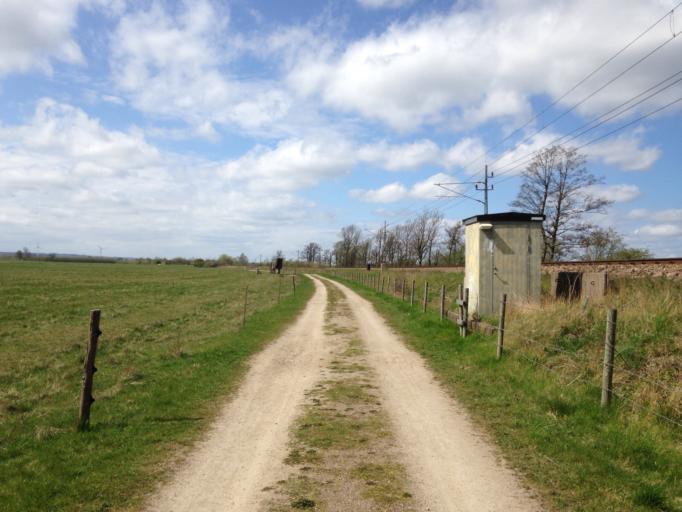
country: SE
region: Skane
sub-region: Kristianstads Kommun
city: Kristianstad
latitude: 56.0410
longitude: 14.1390
